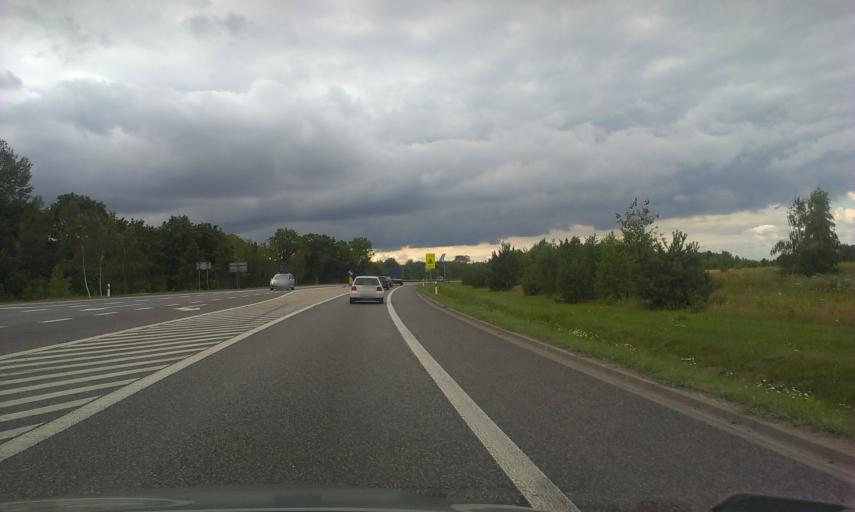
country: PL
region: Masovian Voivodeship
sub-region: Powiat zyrardowski
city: Mszczonow
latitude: 51.9940
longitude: 20.5013
